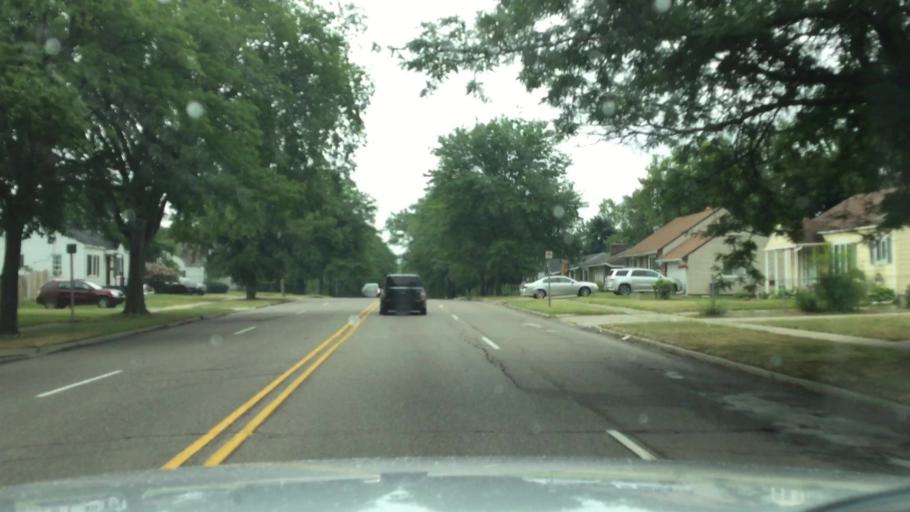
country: US
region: Michigan
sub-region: Genesee County
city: Flint
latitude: 43.0090
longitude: -83.7291
